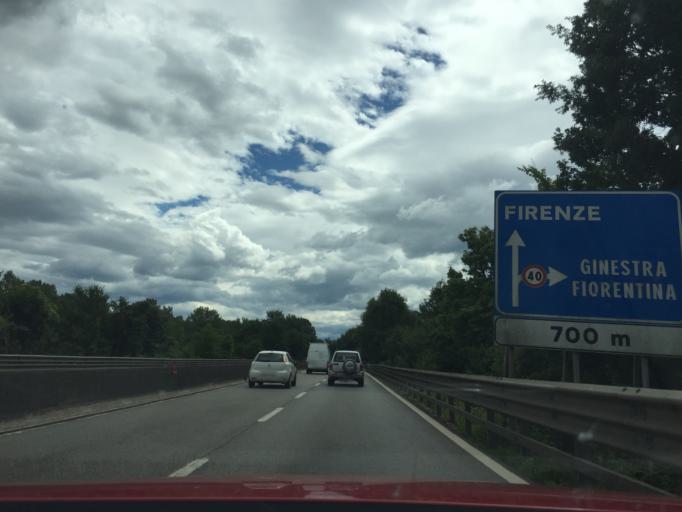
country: IT
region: Tuscany
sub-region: Province of Florence
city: Ginestra Fiorentina
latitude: 43.7118
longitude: 11.0484
